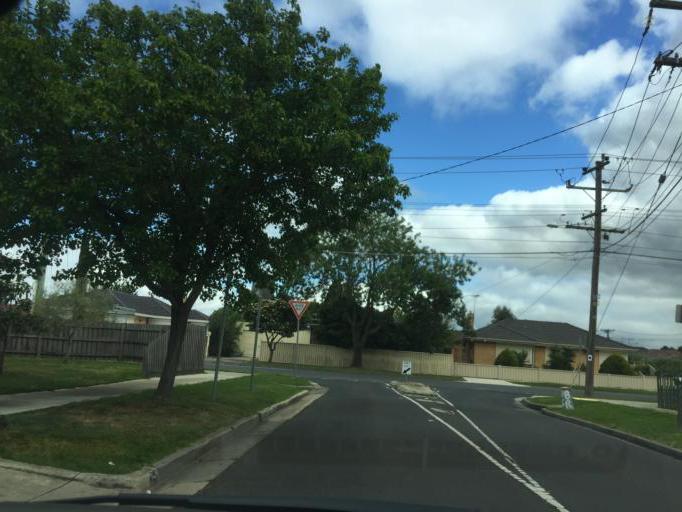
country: AU
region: Victoria
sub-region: Brimbank
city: Sunshine West
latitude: -37.7941
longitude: 144.8192
